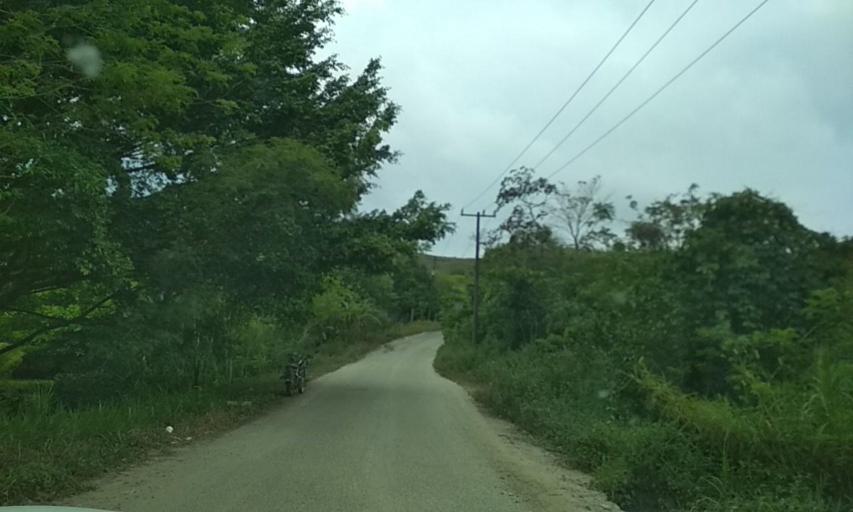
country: MX
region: Veracruz
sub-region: Uxpanapa
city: Poblado 10
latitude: 17.4953
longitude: -94.1383
